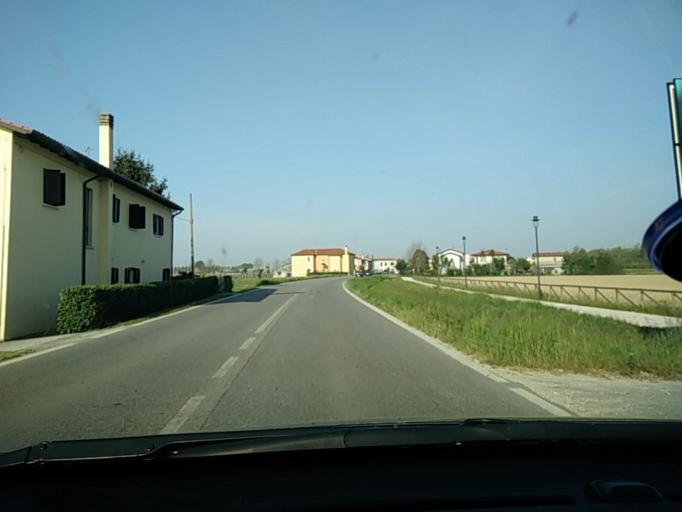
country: IT
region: Veneto
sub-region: Provincia di Treviso
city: Talponada
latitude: 45.7016
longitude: 12.5061
